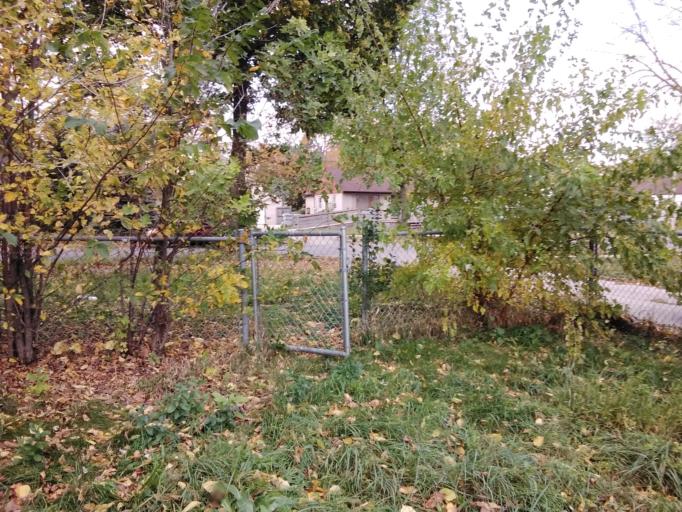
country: US
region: Wisconsin
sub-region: Milwaukee County
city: Glendale
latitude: 43.1030
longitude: -87.9690
